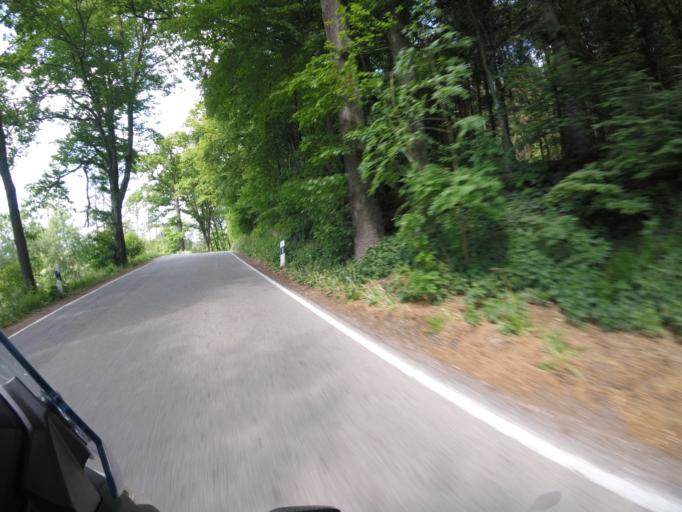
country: DE
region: Bavaria
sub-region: Upper Bavaria
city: Wolfersdorf
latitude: 48.4584
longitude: 11.7326
